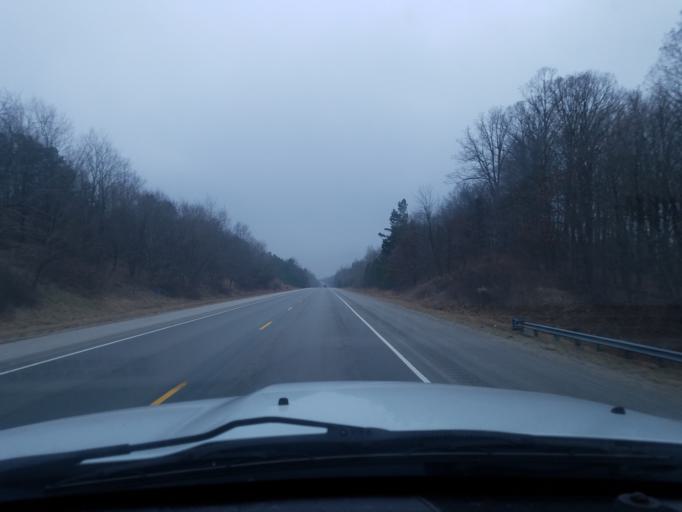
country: US
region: Indiana
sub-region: Crawford County
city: English
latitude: 38.1920
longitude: -86.6001
